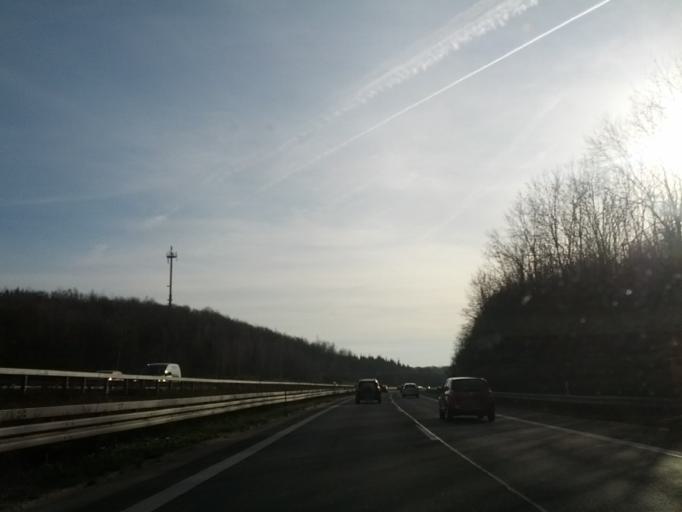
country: DE
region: Bavaria
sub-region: Regierungsbezirk Unterfranken
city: Kurnach
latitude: 49.8309
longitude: 10.0392
